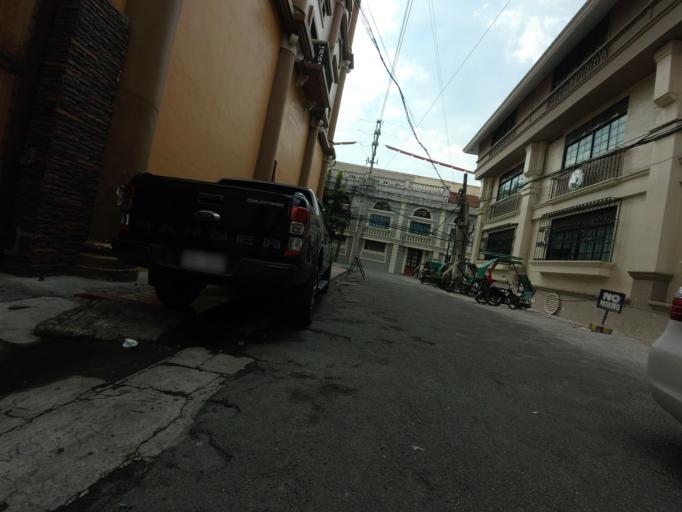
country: PH
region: Metro Manila
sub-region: City of Manila
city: Port Area
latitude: 14.5872
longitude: 120.9776
